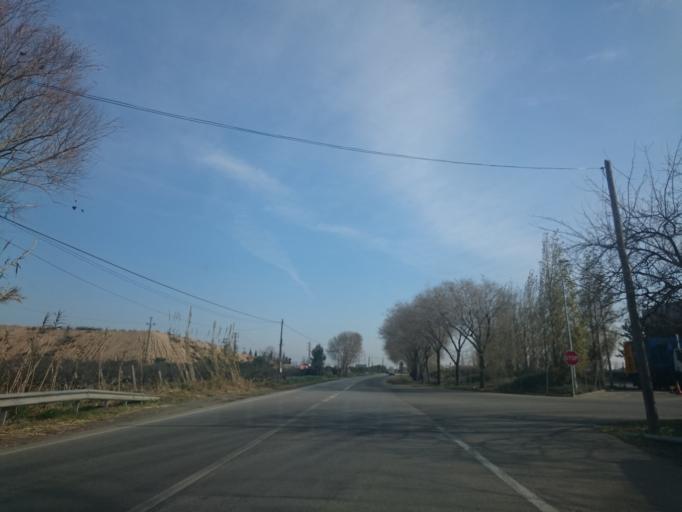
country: ES
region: Catalonia
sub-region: Provincia de Barcelona
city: Viladecans
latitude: 41.2981
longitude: 2.0314
